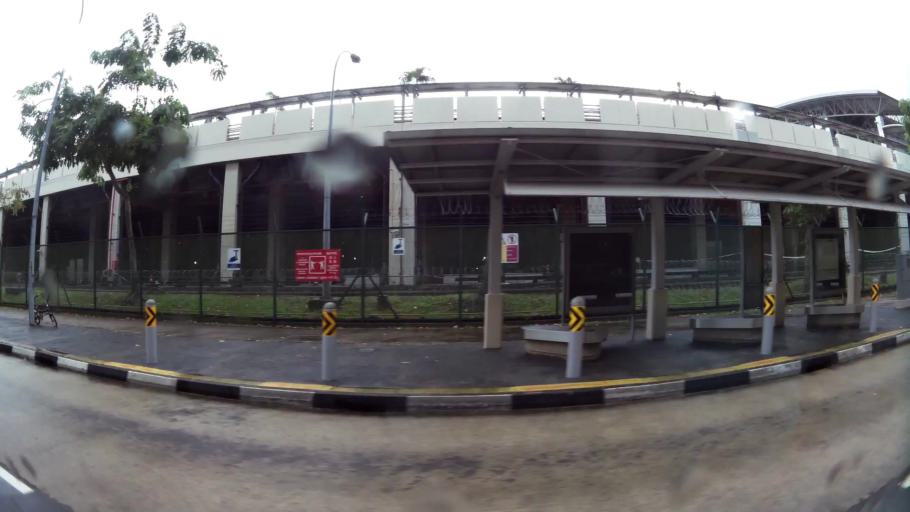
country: MY
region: Johor
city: Kampung Pasir Gudang Baru
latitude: 1.3900
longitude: 103.8846
